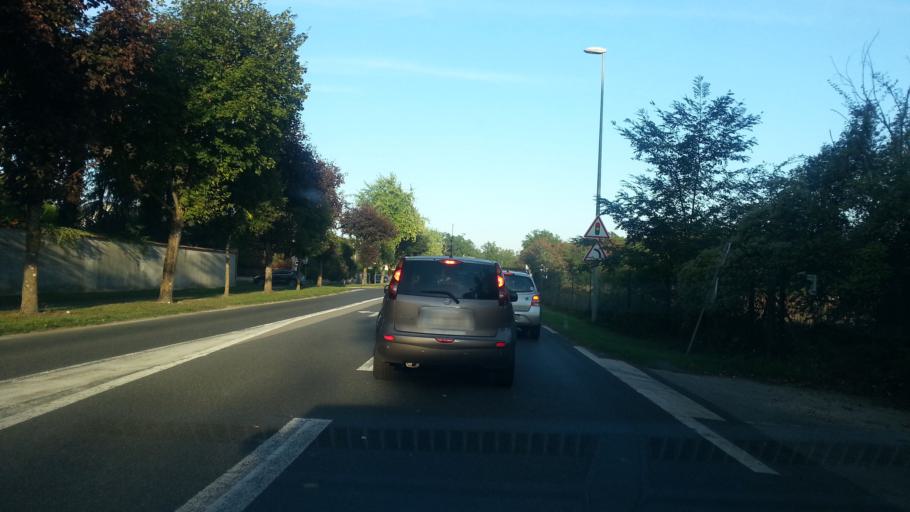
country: FR
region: Picardie
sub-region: Departement de l'Oise
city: Compiegne
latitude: 49.4004
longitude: 2.8233
